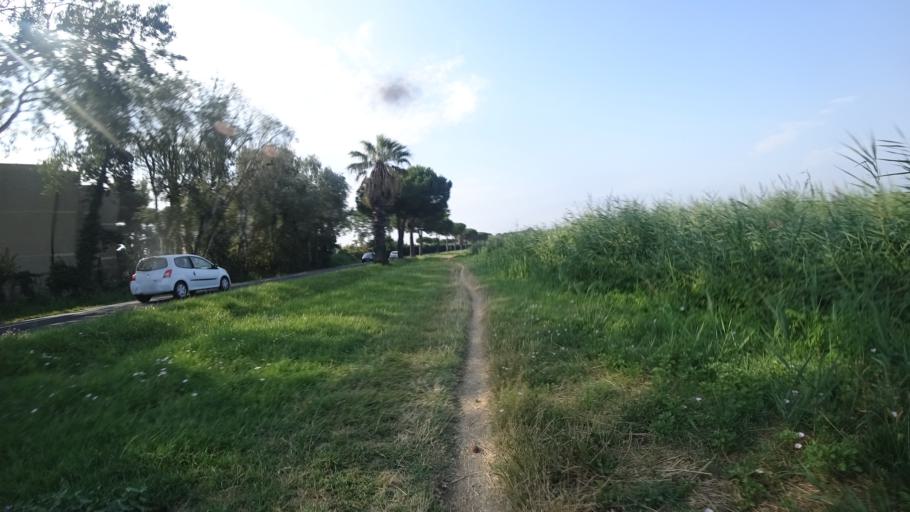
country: FR
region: Languedoc-Roussillon
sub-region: Departement des Pyrenees-Orientales
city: Canet-en-Roussillon
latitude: 42.6951
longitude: 3.0251
